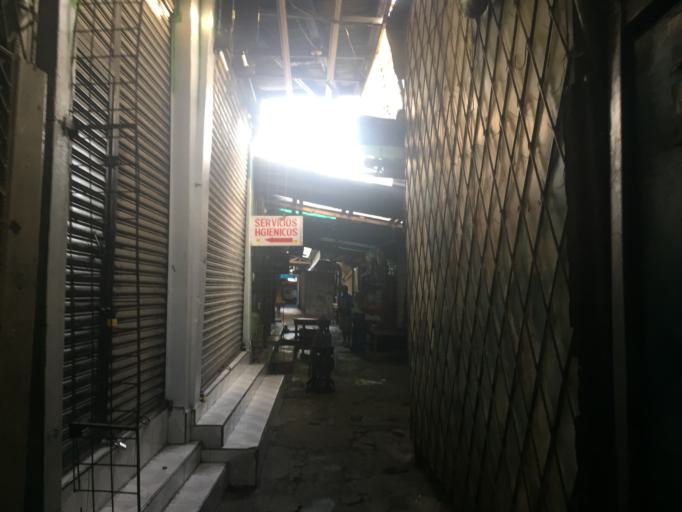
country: NI
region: Managua
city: Managua
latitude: 12.1498
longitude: -86.2595
